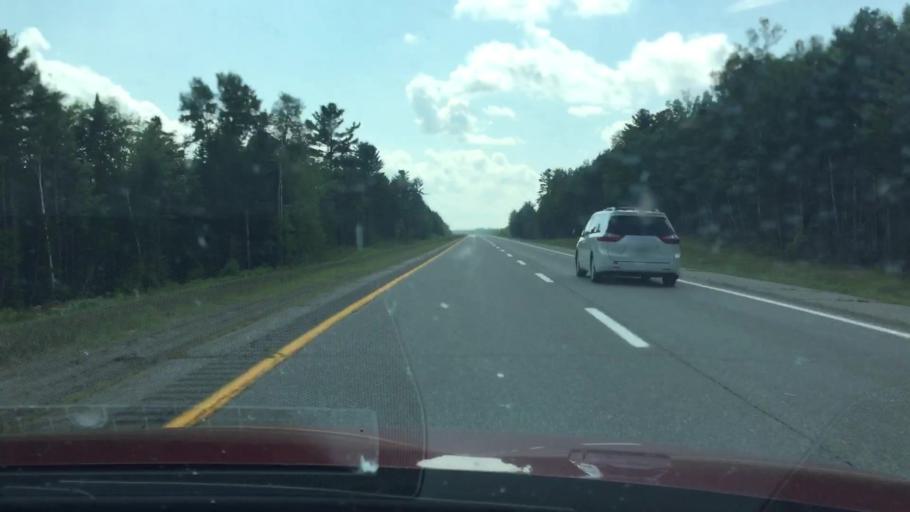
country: US
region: Maine
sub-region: Penobscot County
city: Medway
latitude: 45.4842
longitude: -68.5712
